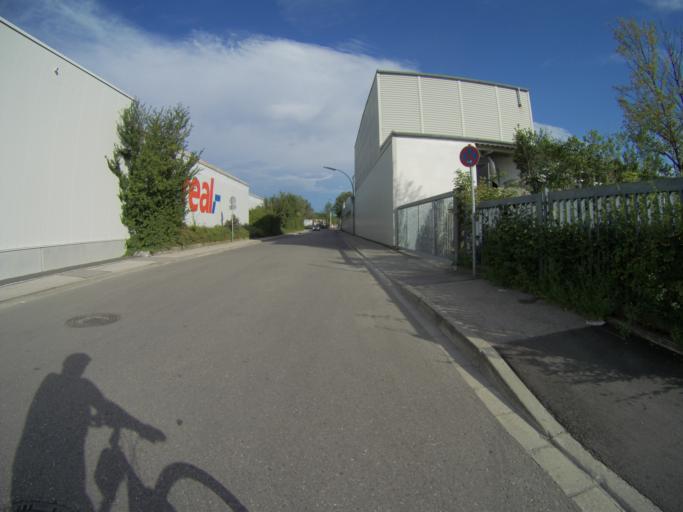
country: DE
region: Bavaria
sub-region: Upper Bavaria
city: Freising
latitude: 48.3874
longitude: 11.7309
